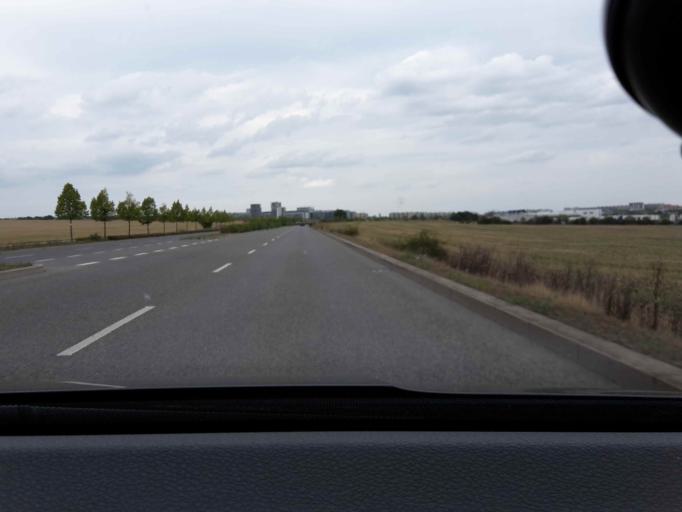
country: CZ
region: Central Bohemia
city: Rudna
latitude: 50.0334
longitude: 14.2852
